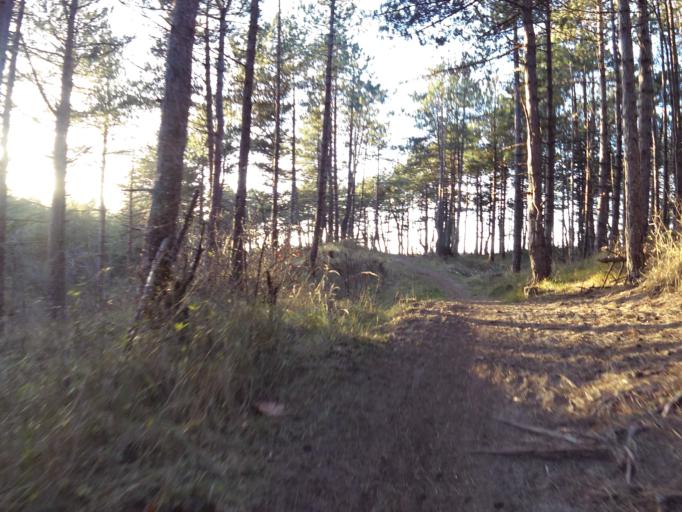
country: NL
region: South Holland
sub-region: Gemeente Noordwijk
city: Noordwijk-Binnen
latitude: 52.2652
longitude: 4.4580
